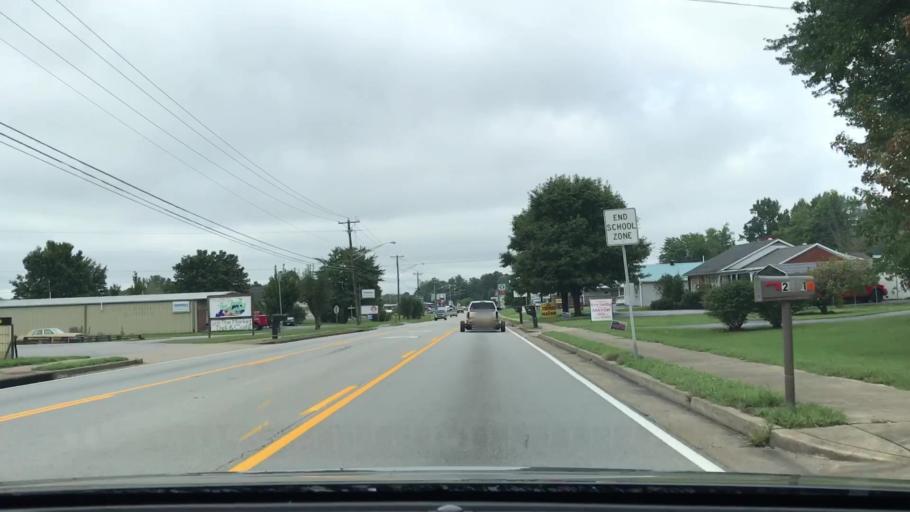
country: US
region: Kentucky
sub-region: Russell County
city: Russell Springs
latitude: 37.0323
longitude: -85.0765
